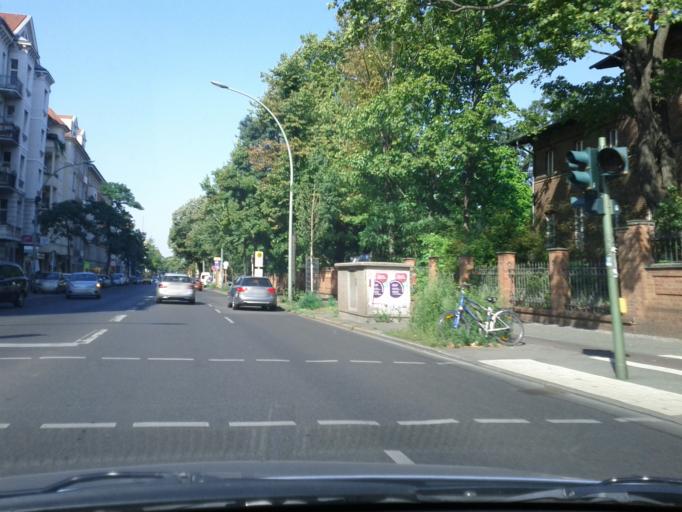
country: DE
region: Berlin
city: Hansaviertel
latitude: 52.5247
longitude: 13.3493
